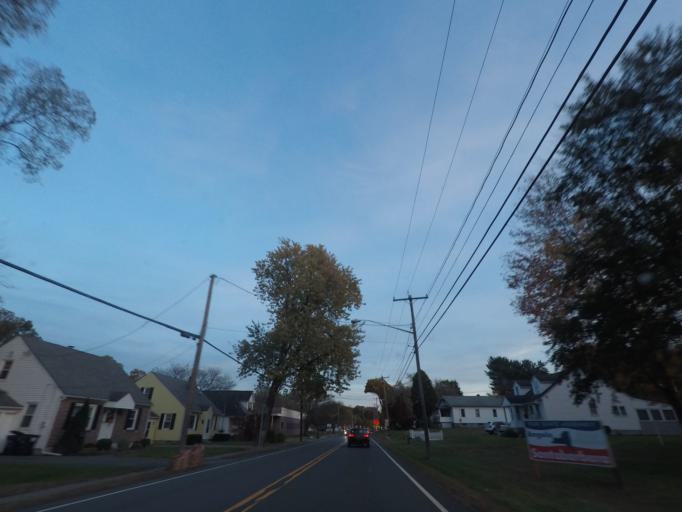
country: US
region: New York
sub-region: Schenectady County
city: Rotterdam
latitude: 42.7666
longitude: -73.9409
